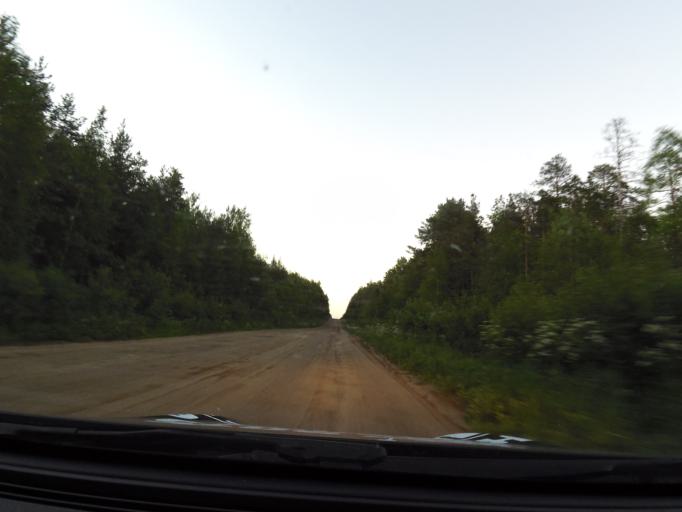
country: RU
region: Leningrad
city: Voznesen'ye
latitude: 60.8593
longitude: 35.9365
